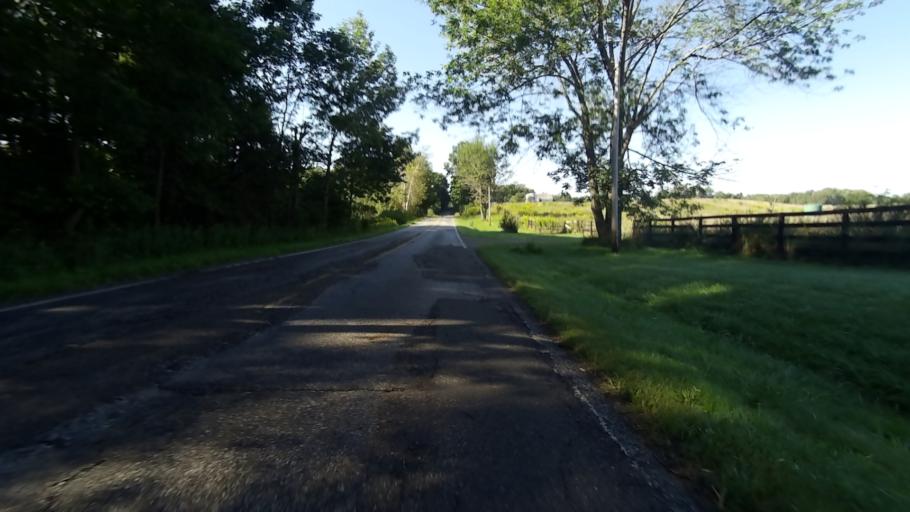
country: US
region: Ohio
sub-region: Portage County
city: Streetsboro
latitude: 41.2088
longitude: -81.3200
